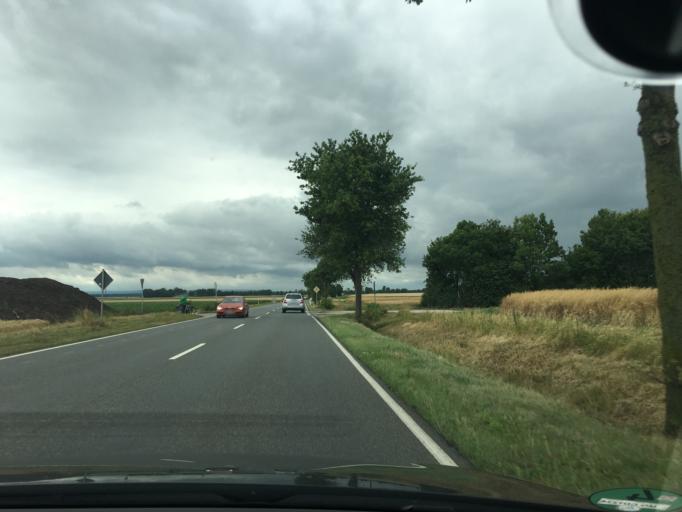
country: DE
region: North Rhine-Westphalia
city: Zulpich
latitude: 50.7333
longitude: 6.6560
